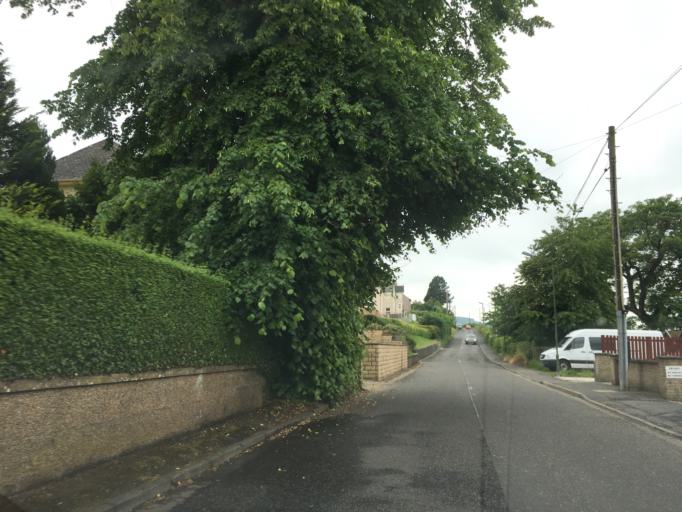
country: GB
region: Scotland
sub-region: Stirling
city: Stirling
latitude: 56.1092
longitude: -3.9707
